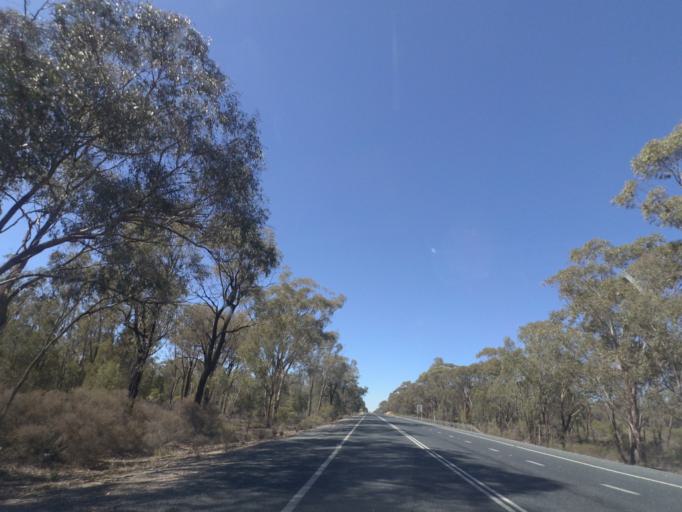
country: AU
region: New South Wales
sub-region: Bland
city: West Wyalong
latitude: -34.1254
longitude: 147.1257
